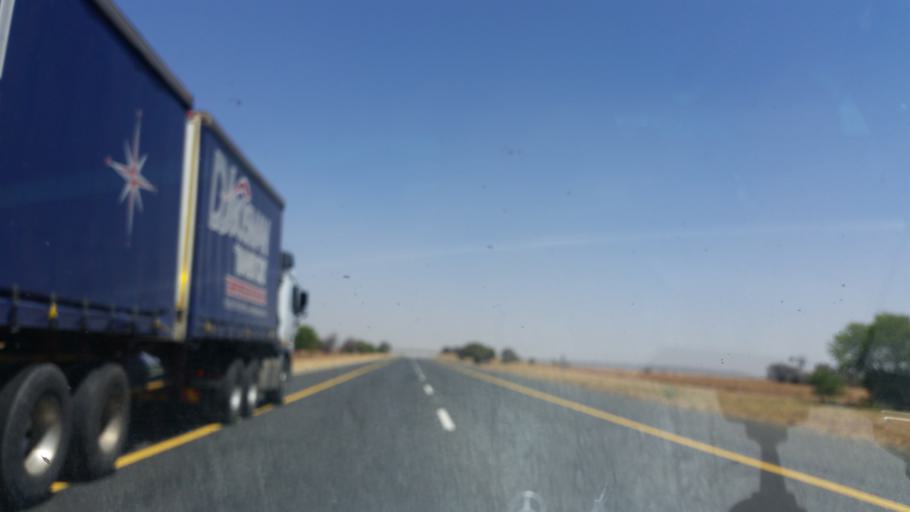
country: ZA
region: Orange Free State
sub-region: Lejweleputswa District Municipality
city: Winburg
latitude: -28.6499
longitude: 26.8765
